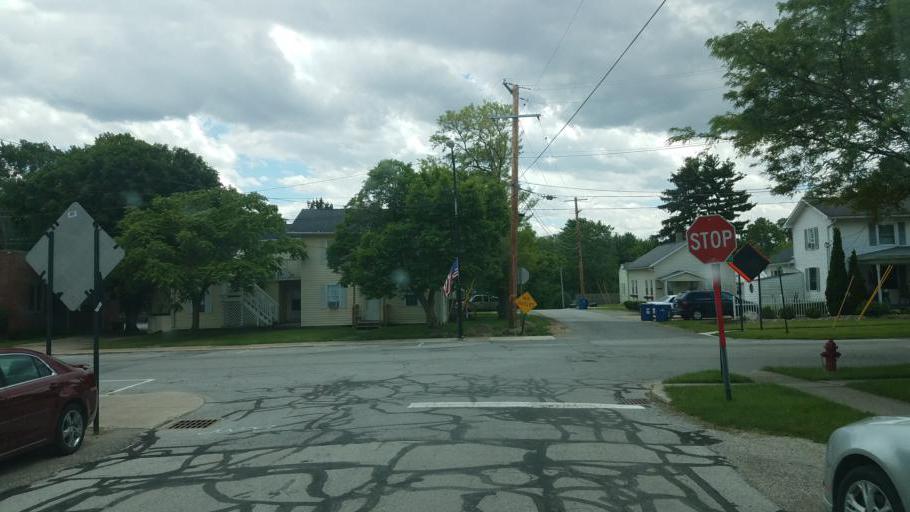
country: US
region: Ohio
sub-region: Huron County
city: Monroeville
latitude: 41.2438
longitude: -82.6964
